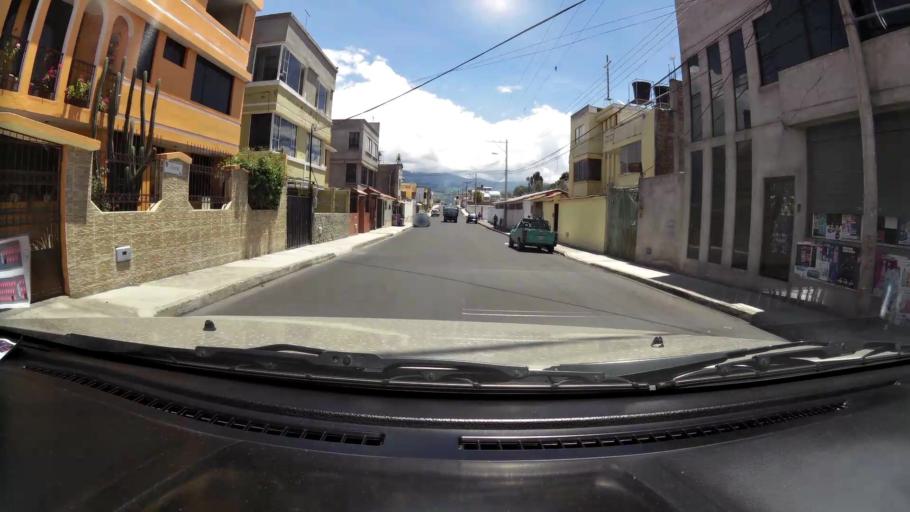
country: EC
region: Chimborazo
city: Riobamba
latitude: -1.6750
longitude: -78.6407
